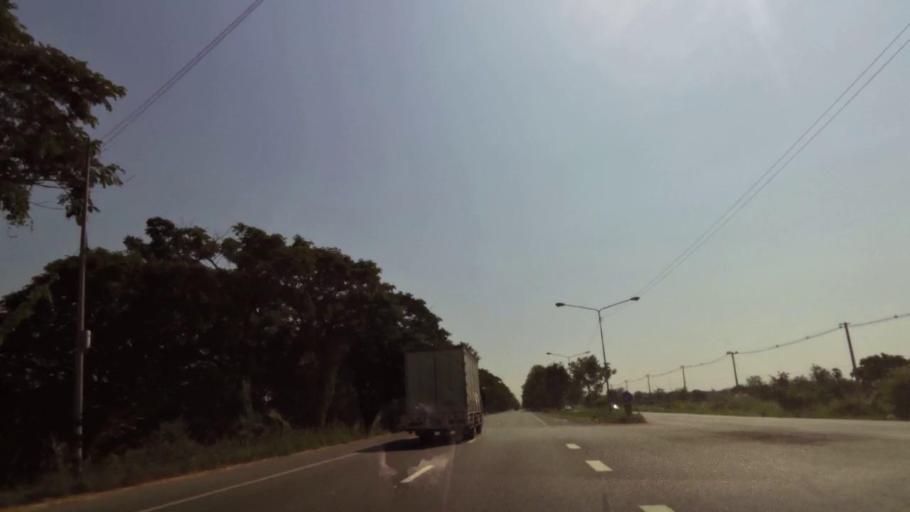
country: TH
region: Nakhon Sawan
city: Kao Liao
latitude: 15.9029
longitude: 100.1130
